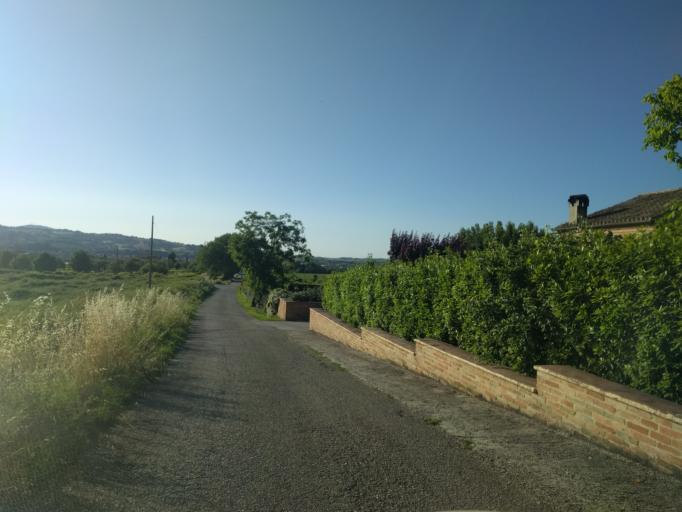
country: IT
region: The Marches
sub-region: Provincia di Pesaro e Urbino
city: Montemaggiore al Metauro
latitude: 43.7403
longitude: 12.9451
